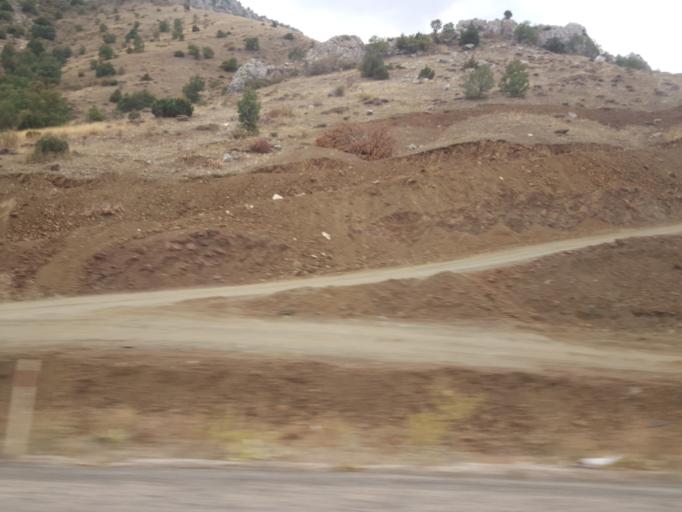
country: TR
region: Yozgat
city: Cekerek
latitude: 40.2093
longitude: 35.4797
